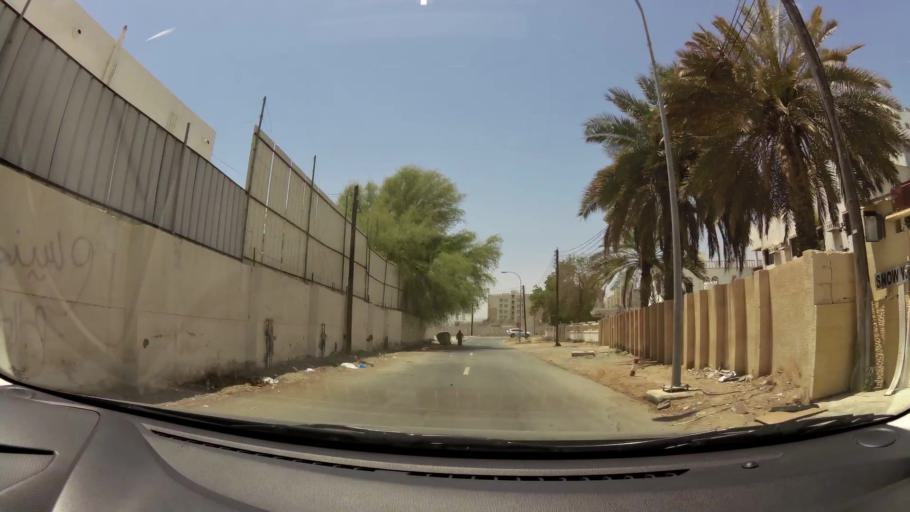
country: OM
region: Muhafazat Masqat
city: As Sib al Jadidah
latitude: 23.6229
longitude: 58.2428
